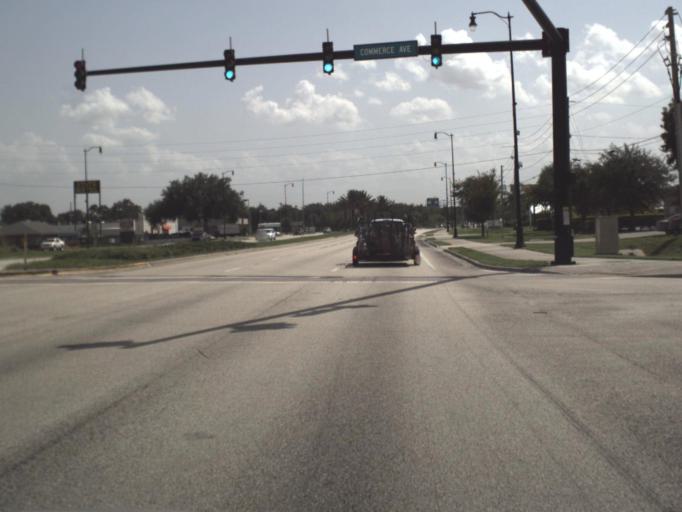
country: US
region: Florida
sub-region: Polk County
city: Haines City
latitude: 28.1177
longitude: -81.6398
